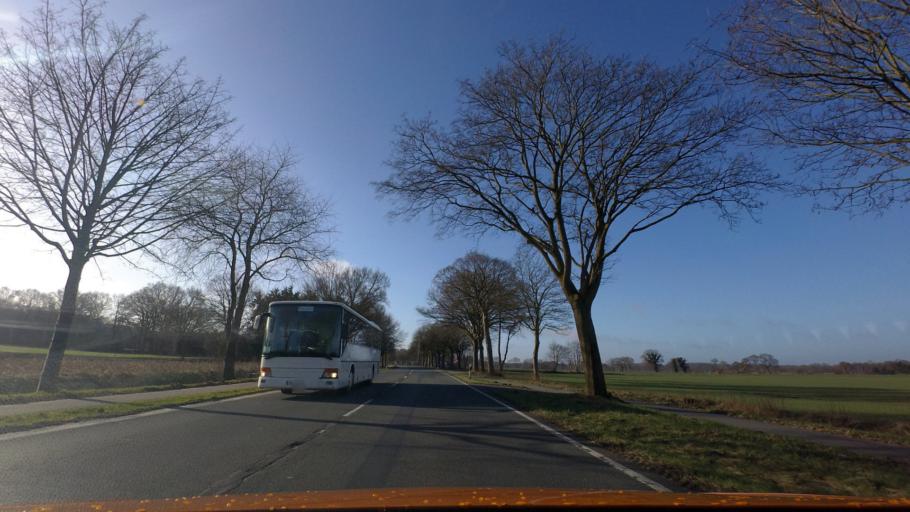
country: DE
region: Lower Saxony
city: Wardenburg
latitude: 53.0820
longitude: 8.1930
